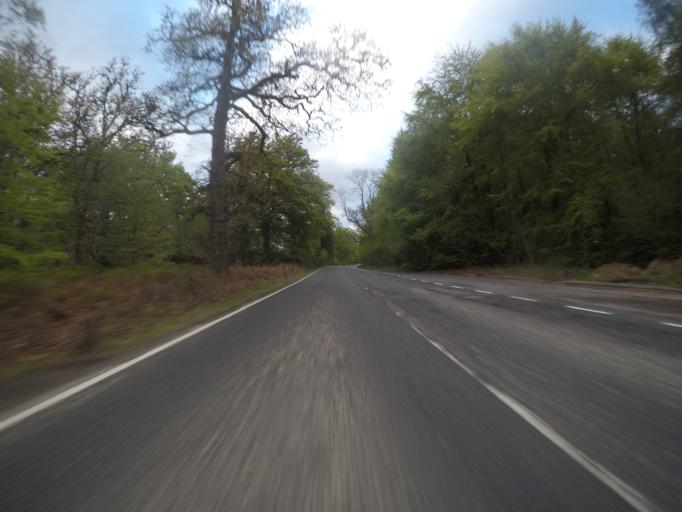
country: GB
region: Scotland
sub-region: Highland
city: Spean Bridge
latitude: 57.0834
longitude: -4.7570
